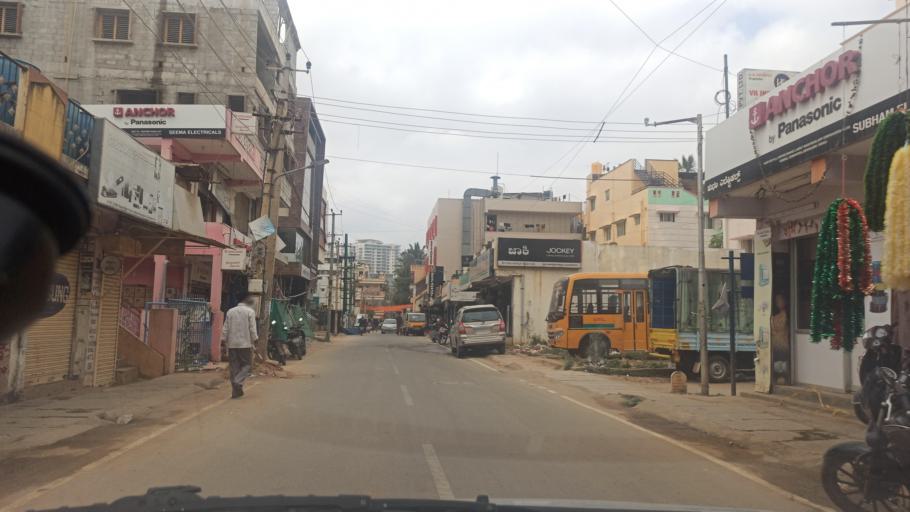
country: IN
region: Karnataka
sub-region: Bangalore Urban
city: Yelahanka
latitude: 13.0495
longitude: 77.6026
